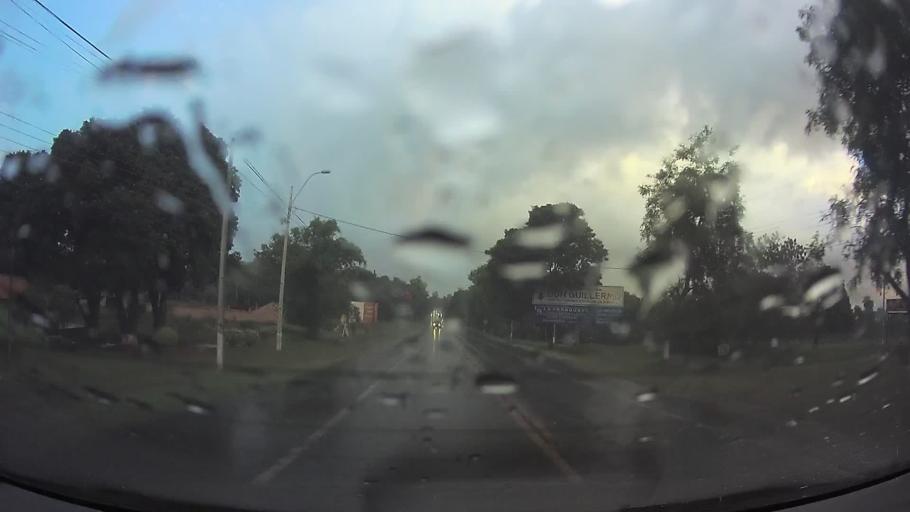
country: PY
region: Paraguari
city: Yaguaron
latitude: -25.5829
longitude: -57.2484
